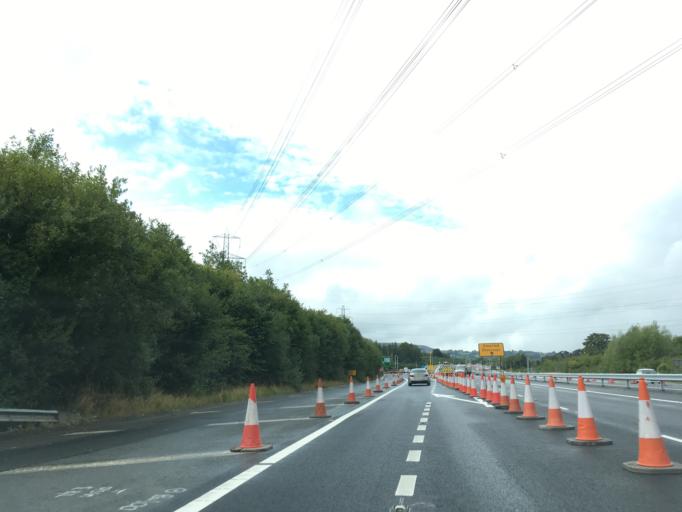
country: GB
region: Wales
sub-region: Monmouthshire
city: Gilwern
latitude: 51.8220
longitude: -3.0691
